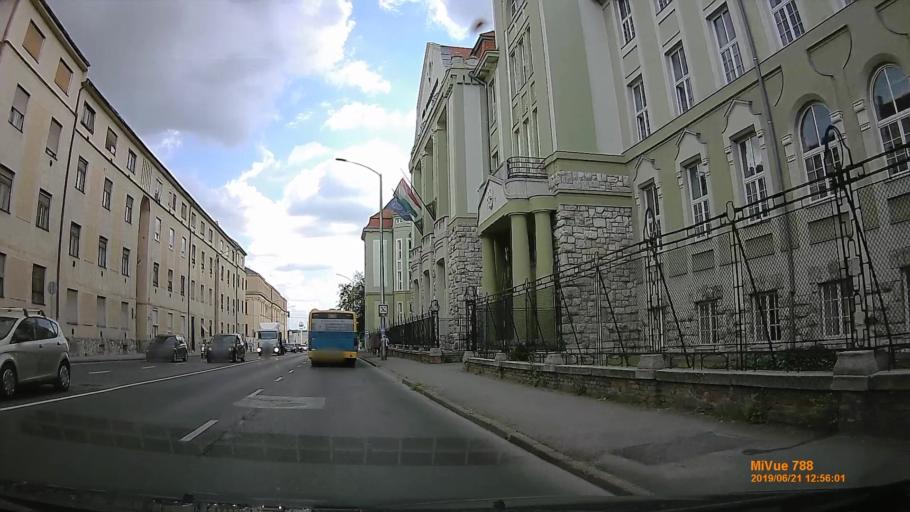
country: HU
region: Baranya
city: Pecs
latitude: 46.0746
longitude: 18.2365
